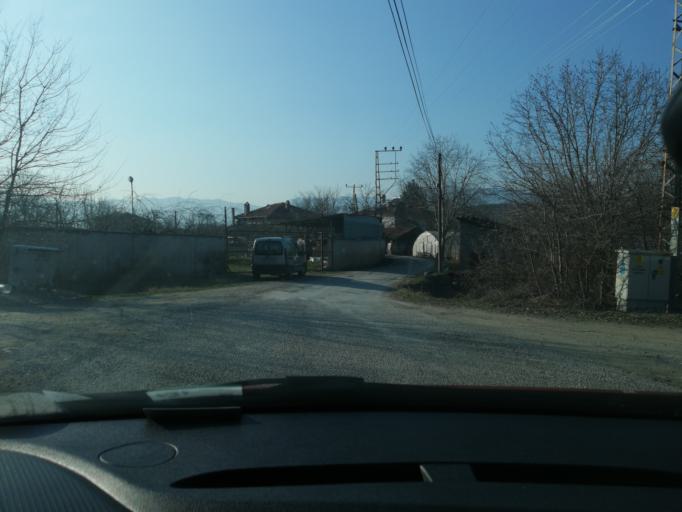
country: TR
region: Karabuk
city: Safranbolu
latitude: 41.2160
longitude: 32.7450
